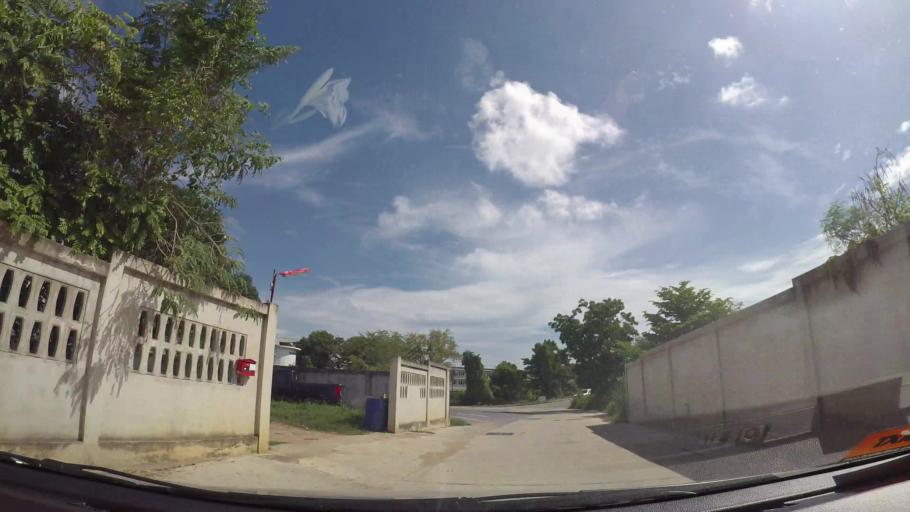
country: TH
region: Chon Buri
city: Sattahip
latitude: 12.6898
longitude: 100.8942
